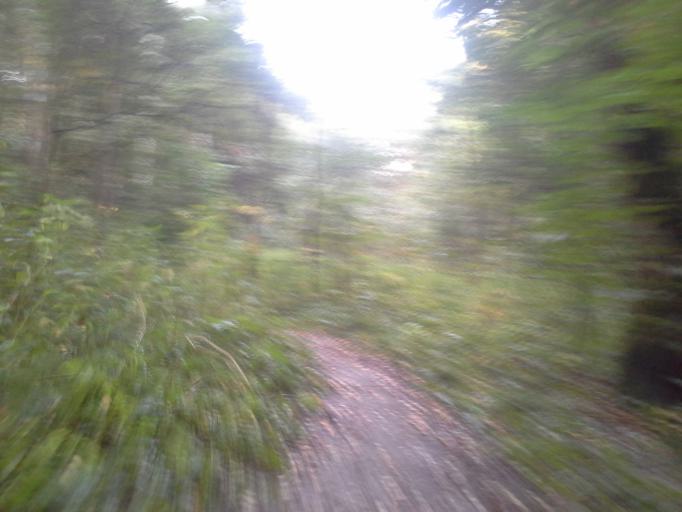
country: RU
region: Moskovskaya
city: Dubrovitsy
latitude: 55.5004
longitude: 37.4388
